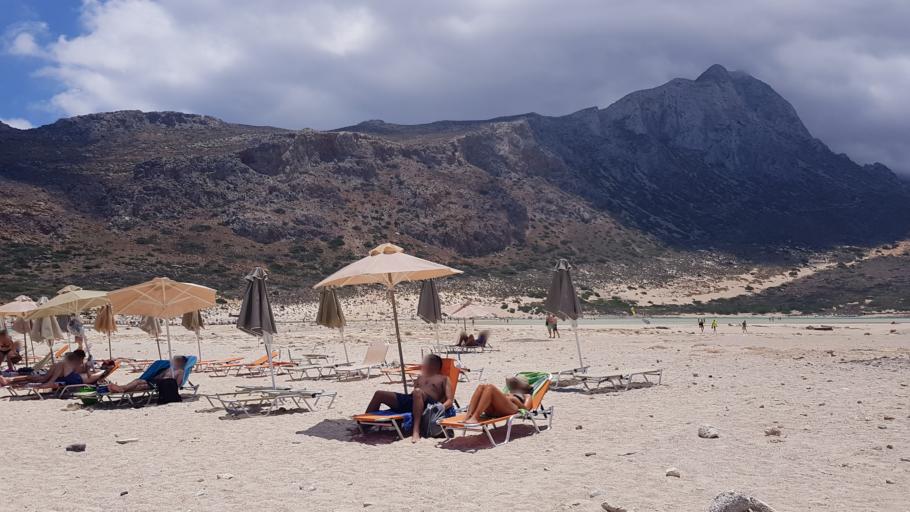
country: GR
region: Crete
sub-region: Nomos Chanias
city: Kissamos
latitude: 35.5852
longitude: 23.5874
